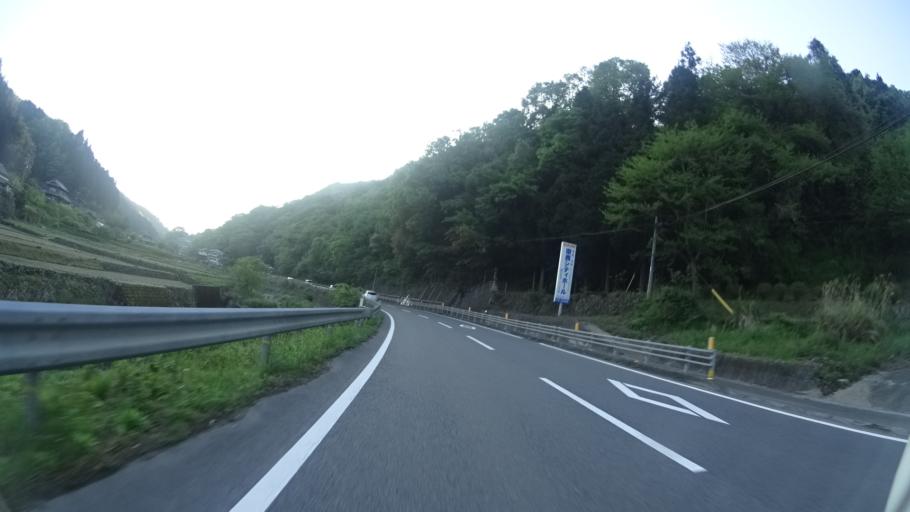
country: JP
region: Tokushima
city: Ikedacho
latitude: 34.0099
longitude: 133.7306
